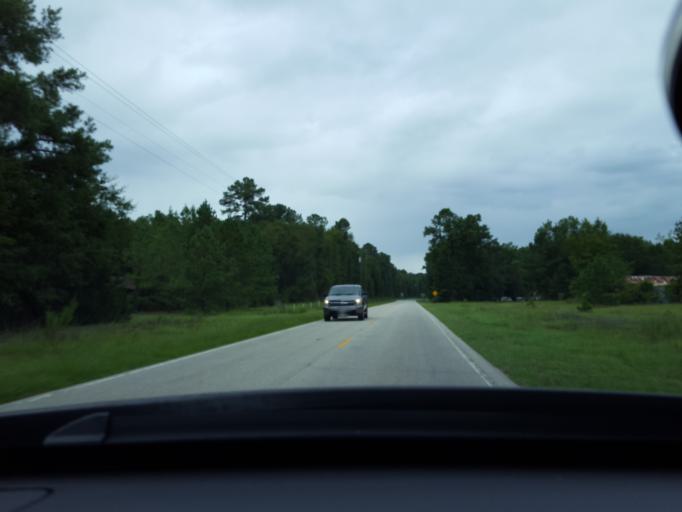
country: US
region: North Carolina
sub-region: Sampson County
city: Clinton
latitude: 34.7812
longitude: -78.3241
